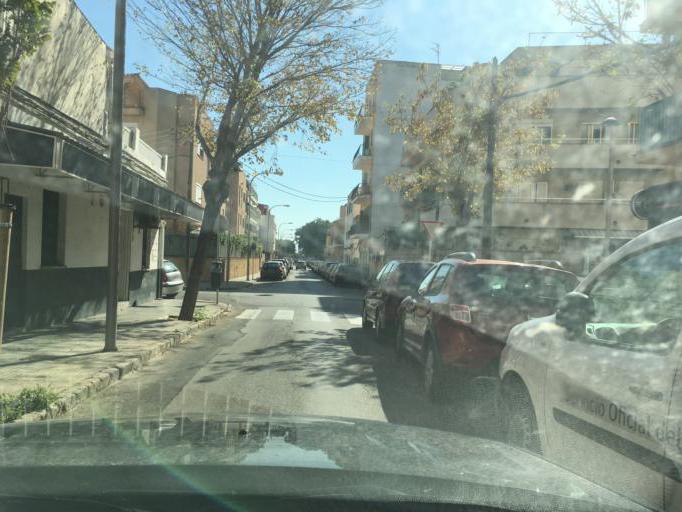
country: ES
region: Balearic Islands
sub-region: Illes Balears
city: Palma
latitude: 39.5836
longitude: 2.6768
